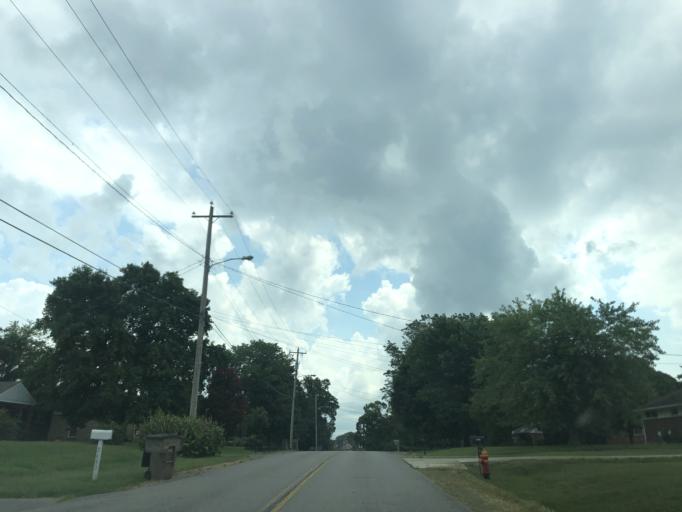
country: US
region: Tennessee
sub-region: Davidson County
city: Lakewood
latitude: 36.1604
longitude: -86.6680
